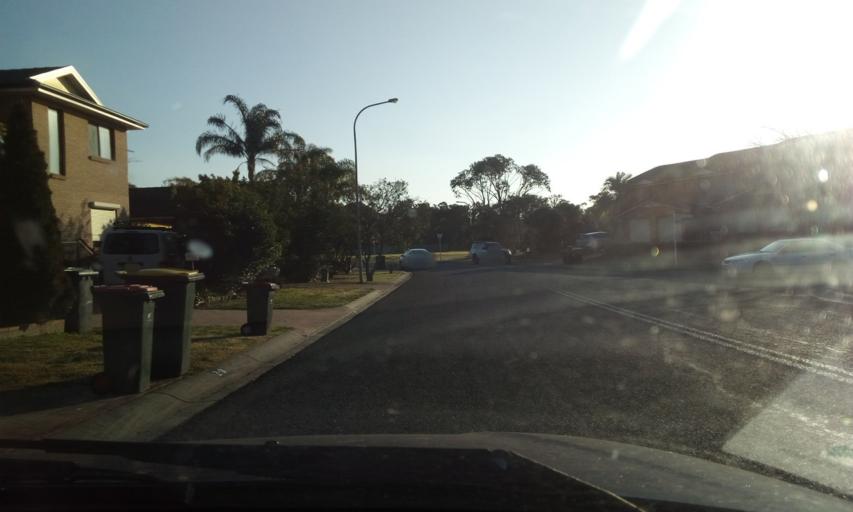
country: AU
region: New South Wales
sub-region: Wollongong
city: Mount Saint Thomas
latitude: -34.4439
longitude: 150.8558
